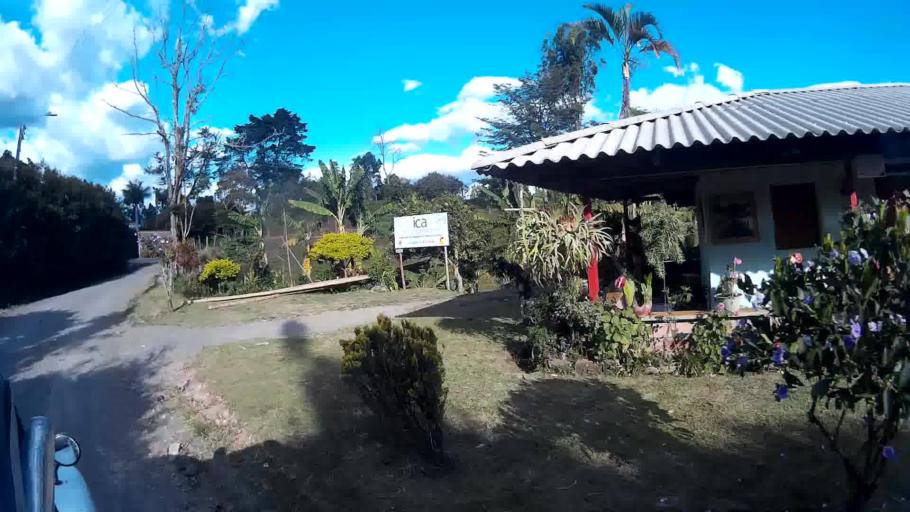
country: CO
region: Quindio
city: Filandia
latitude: 4.7169
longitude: -75.6772
